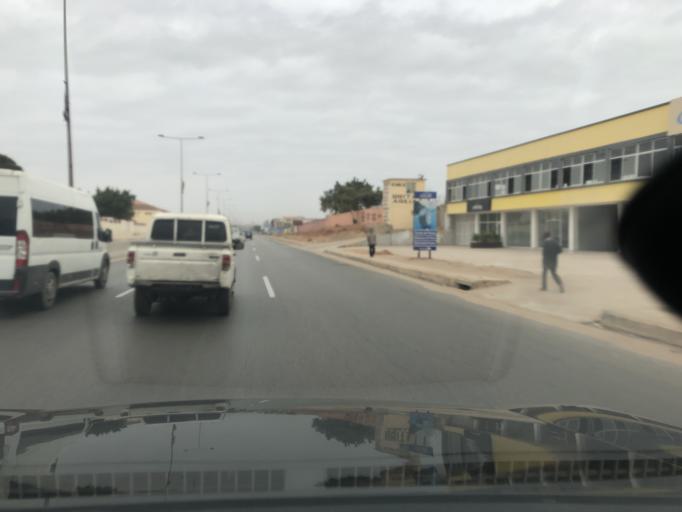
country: AO
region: Luanda
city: Luanda
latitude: -8.9695
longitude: 13.1629
